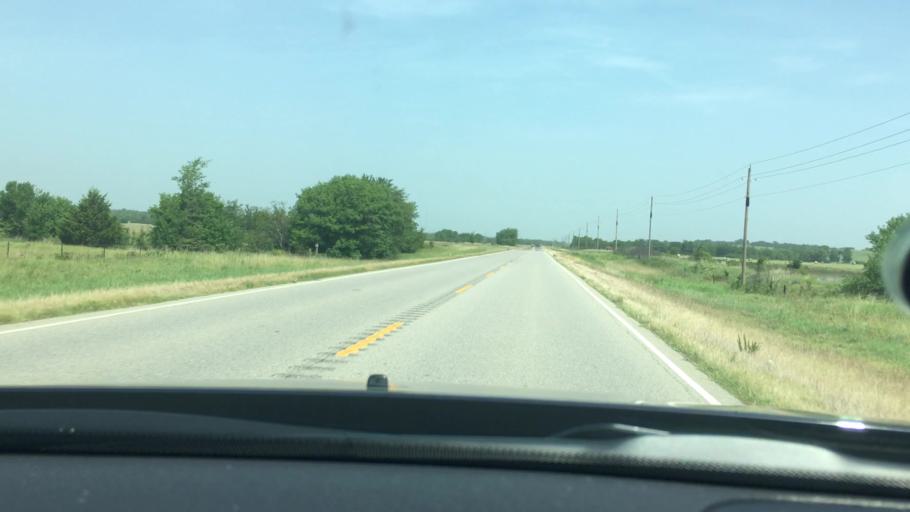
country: US
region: Oklahoma
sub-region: Atoka County
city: Atoka
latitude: 34.4257
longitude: -96.1937
